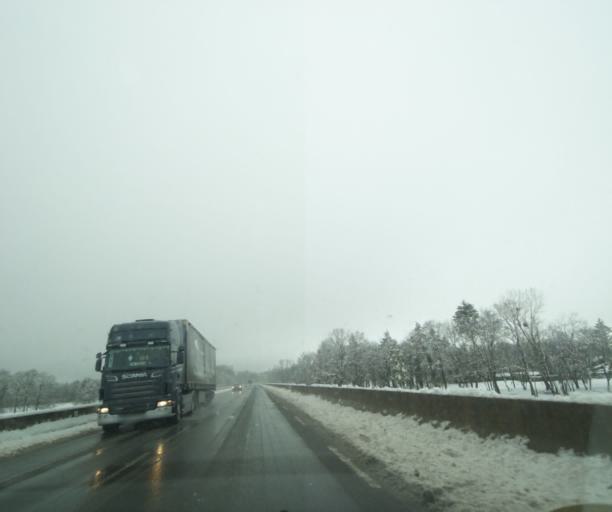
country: FR
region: Champagne-Ardenne
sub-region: Departement de la Haute-Marne
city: Villiers-en-Lieu
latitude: 48.5767
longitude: 4.8694
